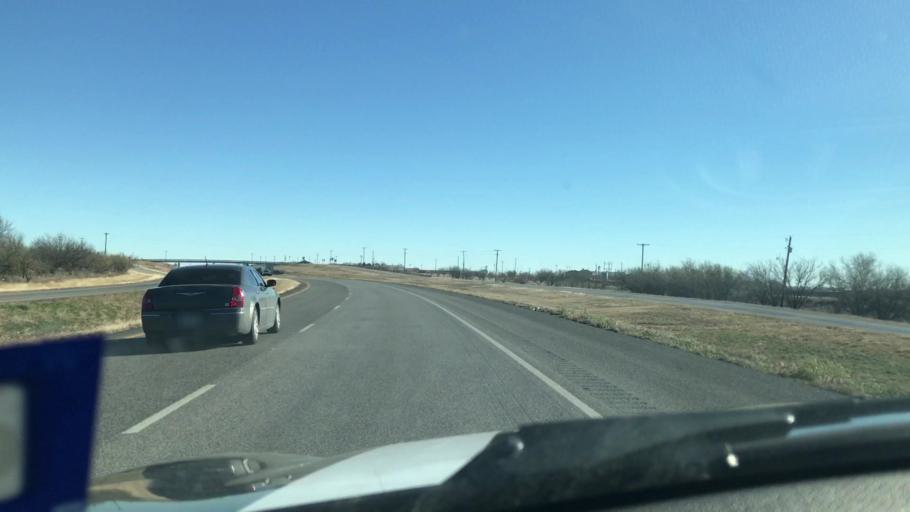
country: US
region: Texas
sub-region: Scurry County
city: Snyder
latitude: 32.7964
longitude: -100.9640
